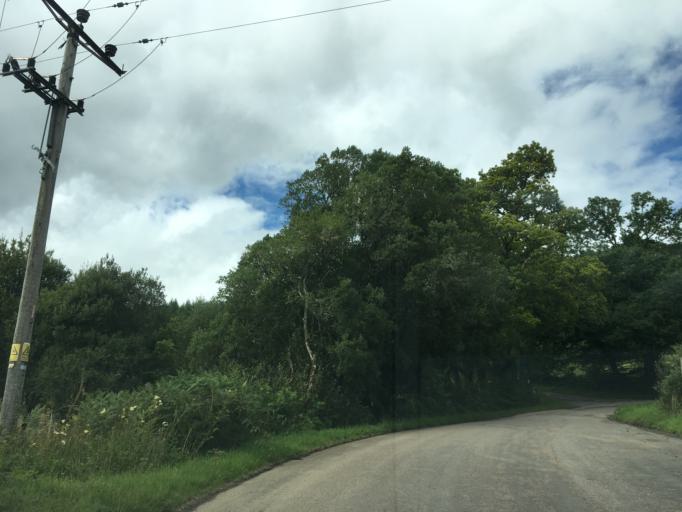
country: GB
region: Scotland
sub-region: Argyll and Bute
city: Oban
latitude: 56.2755
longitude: -5.2786
